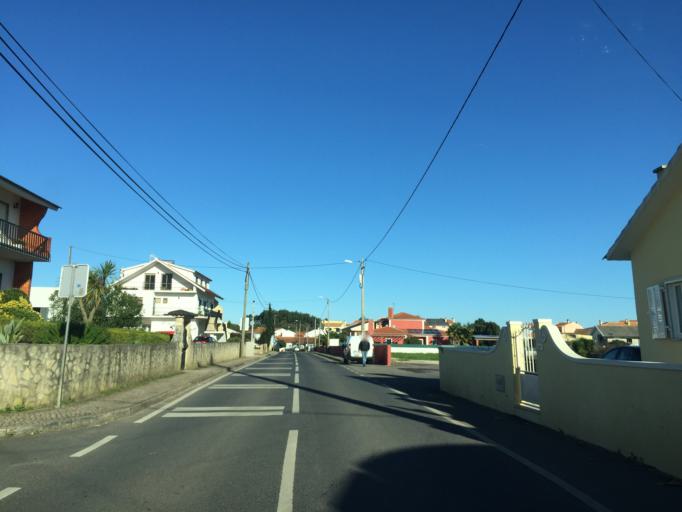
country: PT
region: Lisbon
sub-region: Sintra
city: Almargem
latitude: 38.8392
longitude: -9.2555
